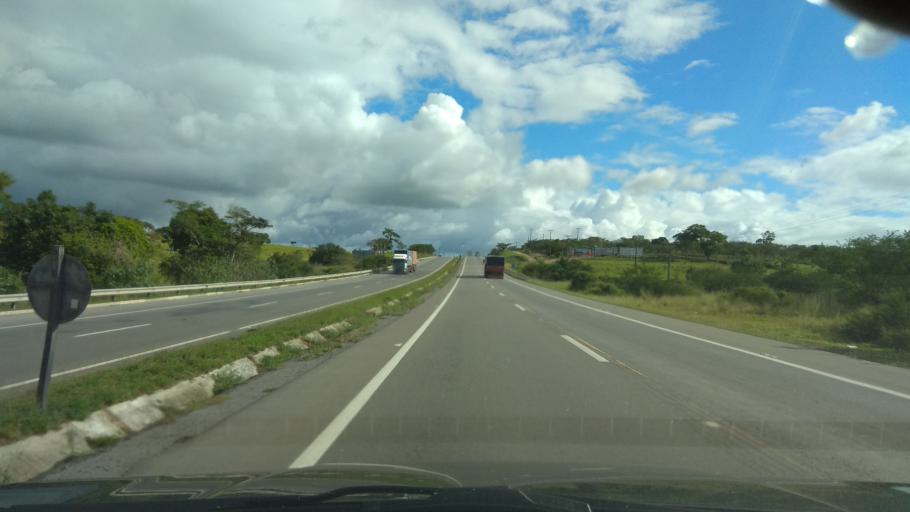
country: BR
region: Bahia
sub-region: Santo Estevao
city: Santo Estevao
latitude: -12.3768
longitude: -39.1226
